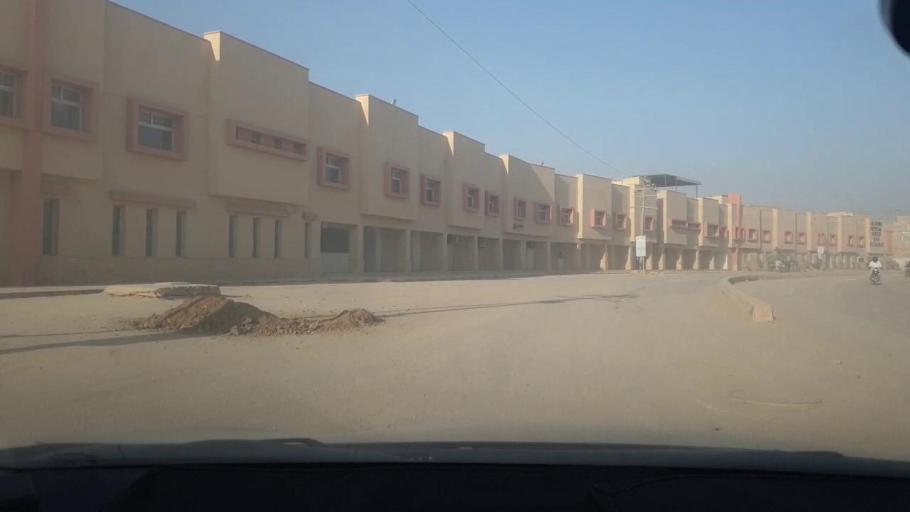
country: PK
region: Sindh
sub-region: Karachi District
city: Karachi
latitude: 24.9769
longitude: 67.0375
